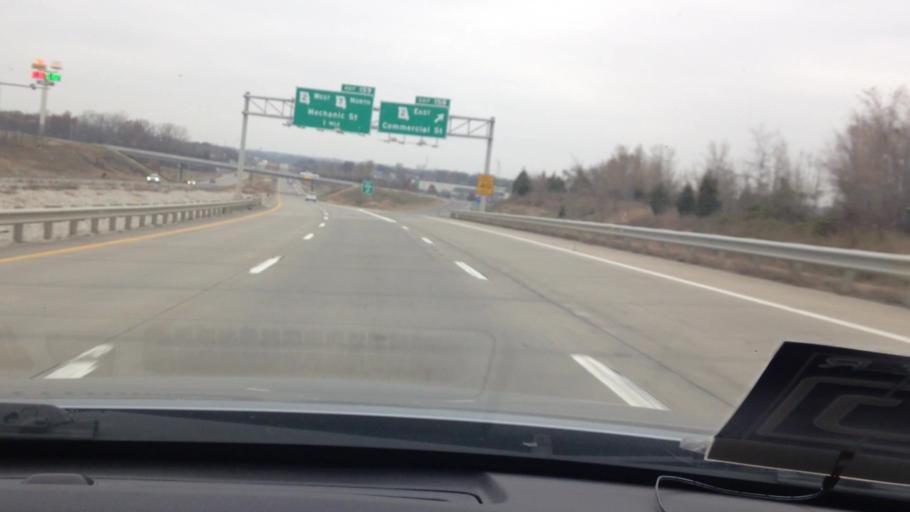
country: US
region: Missouri
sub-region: Cass County
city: Harrisonville
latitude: 38.6346
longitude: -94.3519
